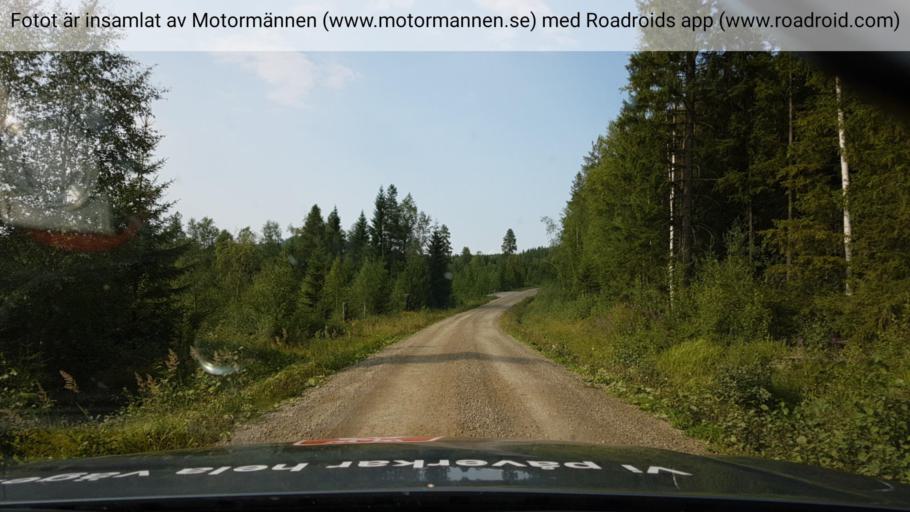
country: SE
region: Jaemtland
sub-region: Bergs Kommun
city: Hoverberg
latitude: 62.5207
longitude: 14.9134
